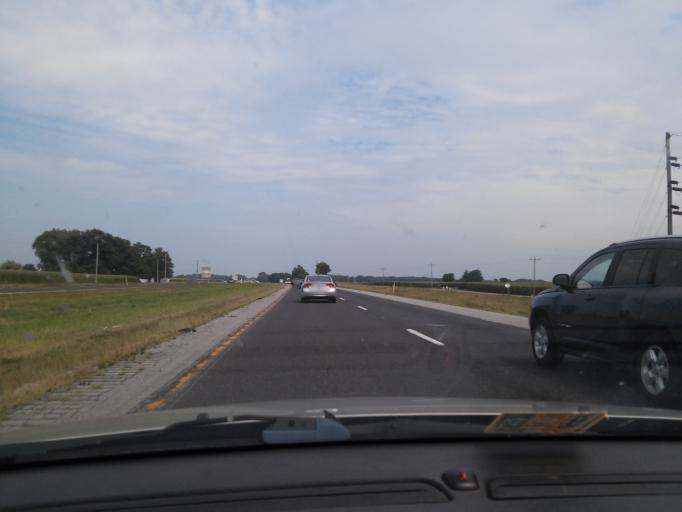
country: US
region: Indiana
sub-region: Wayne County
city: Cambridge City
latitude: 39.8526
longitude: -85.1250
